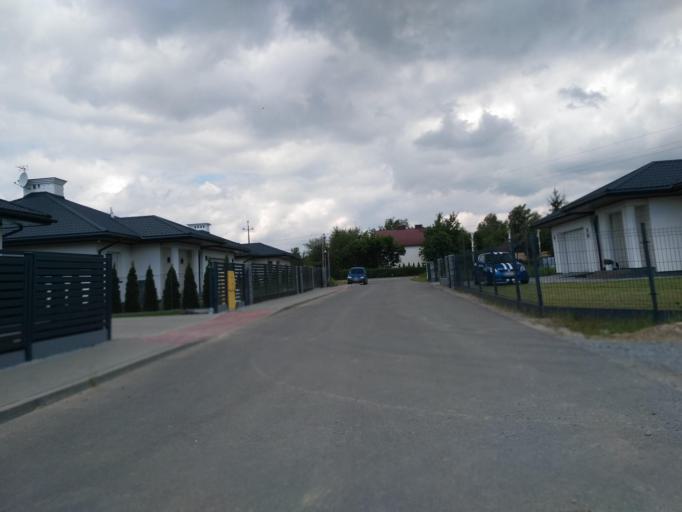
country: PL
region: Subcarpathian Voivodeship
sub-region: Powiat strzyzowski
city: Babica
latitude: 49.9251
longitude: 21.8648
